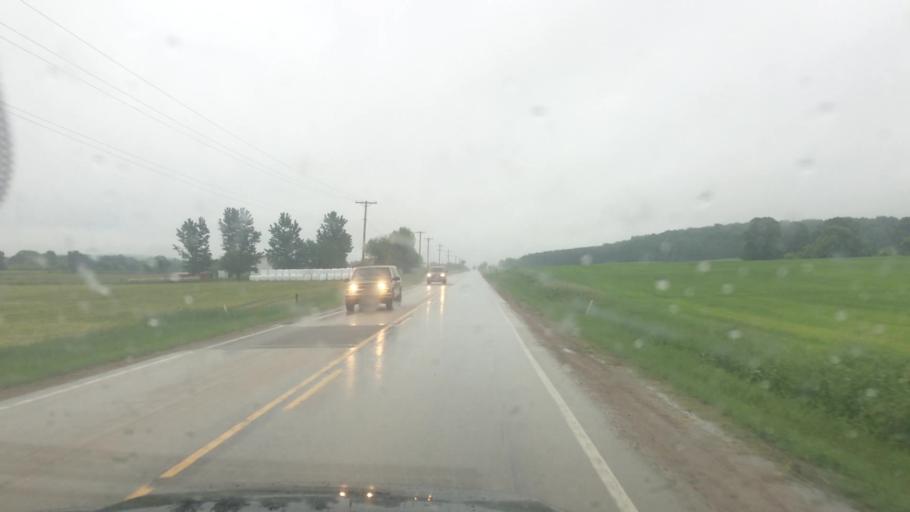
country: US
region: Wisconsin
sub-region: Waupaca County
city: Marion
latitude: 44.6102
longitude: -88.8989
